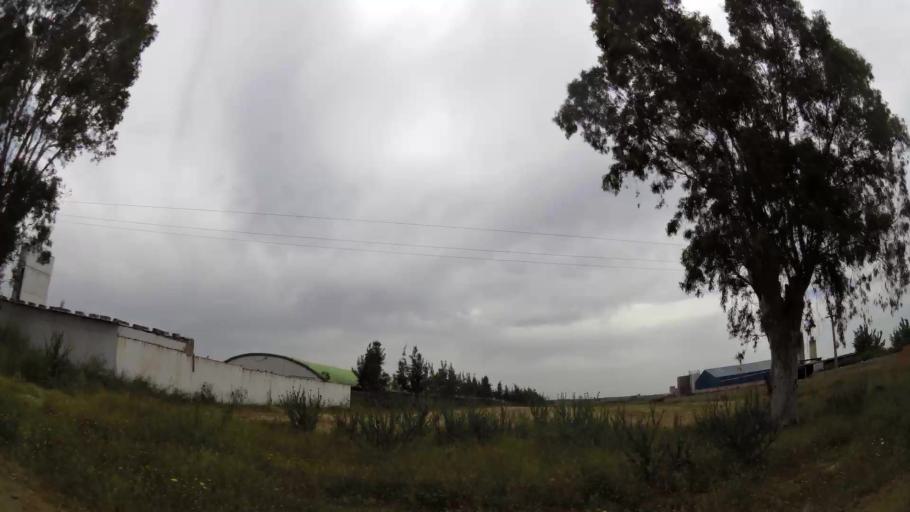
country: MA
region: Rabat-Sale-Zemmour-Zaer
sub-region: Khemisset
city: Tiflet
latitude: 33.8666
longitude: -6.2743
